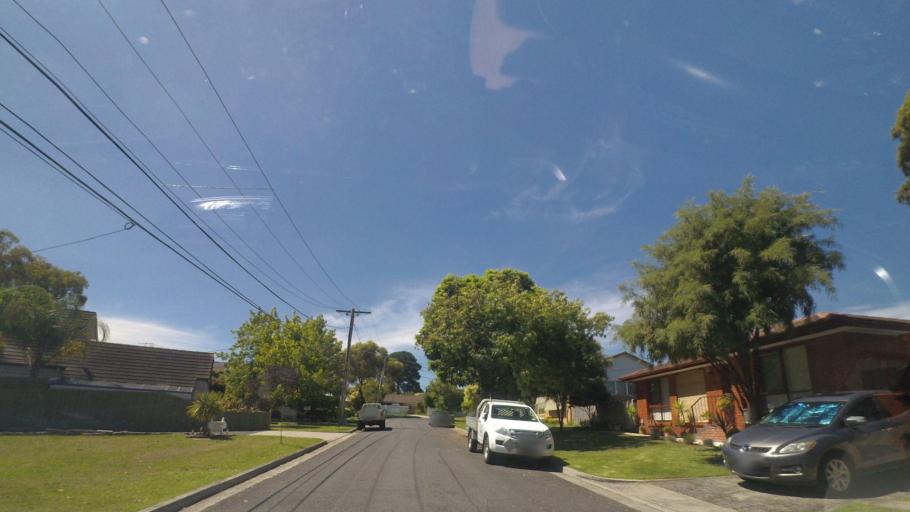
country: AU
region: Victoria
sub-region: Maroondah
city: Ringwood East
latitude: -37.8030
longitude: 145.2288
